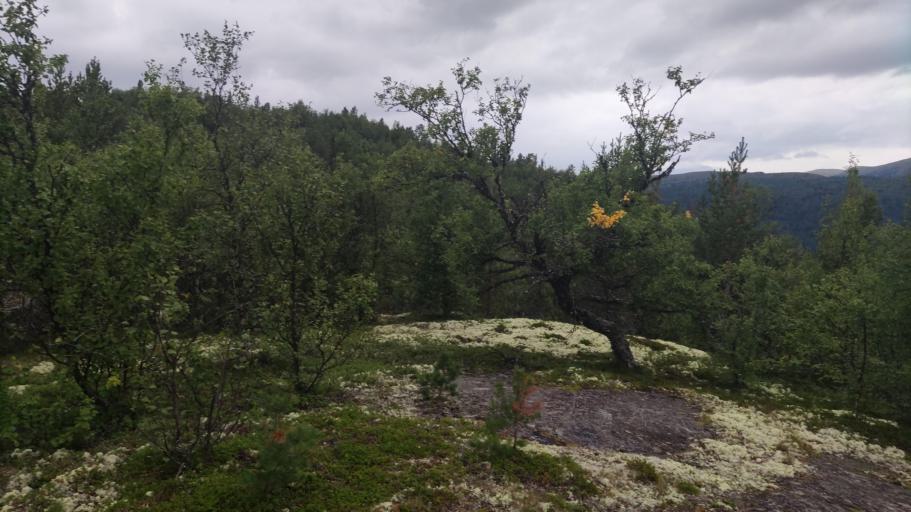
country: NO
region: Oppland
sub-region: Vaga
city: Vagamo
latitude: 61.8039
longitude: 9.2609
